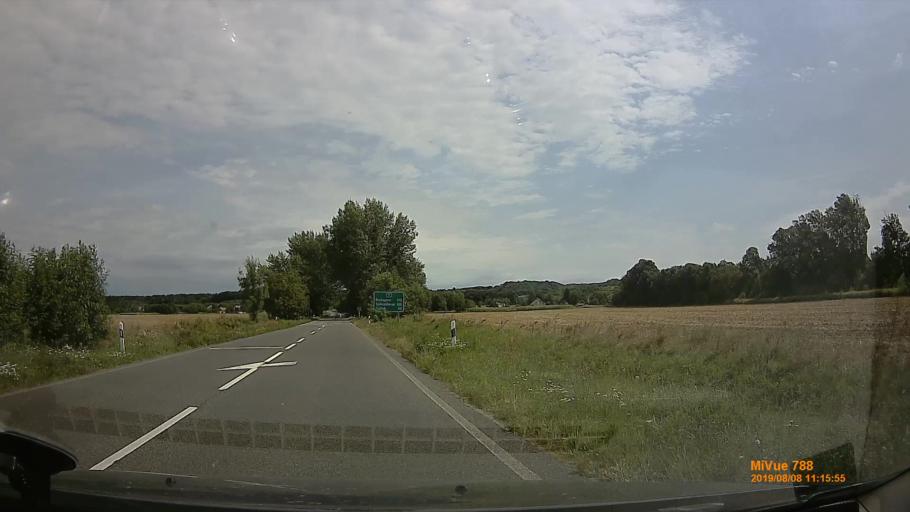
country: HU
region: Somogy
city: Balatonbereny
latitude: 46.6434
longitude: 17.3028
